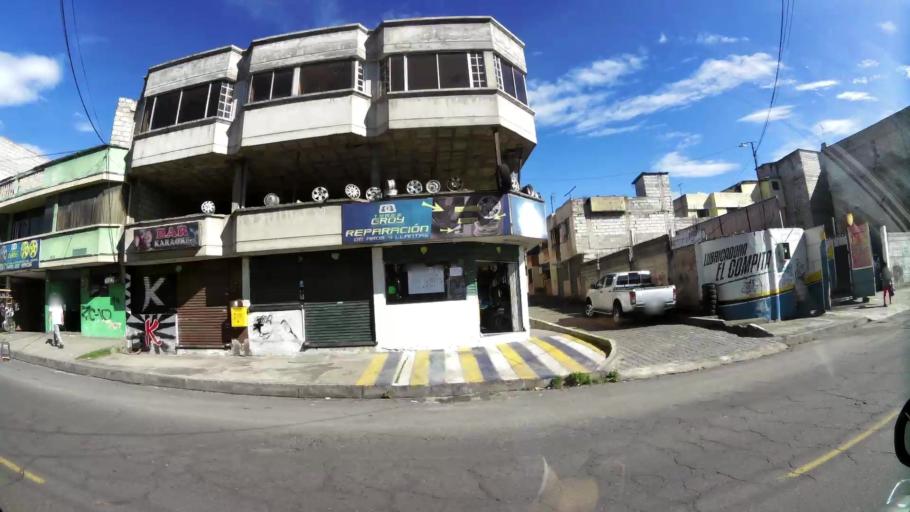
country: EC
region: Pichincha
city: Quito
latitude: -0.2950
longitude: -78.5633
